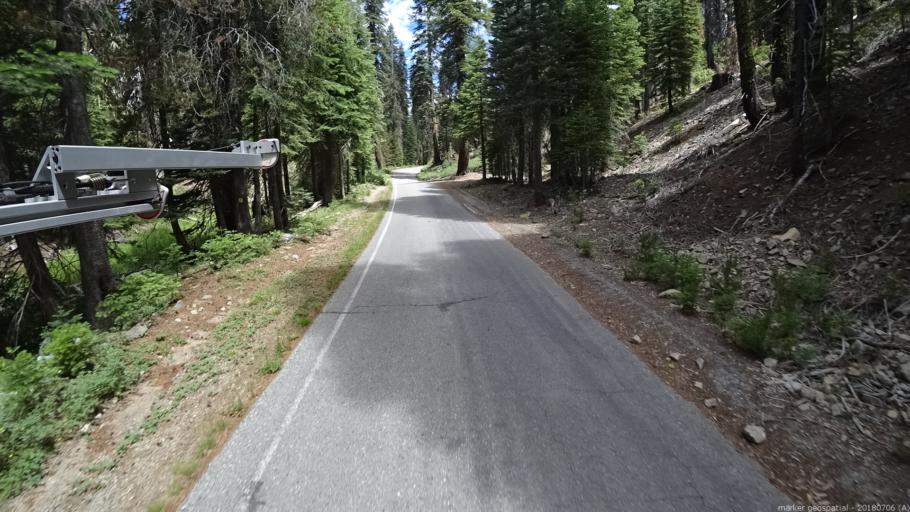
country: US
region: California
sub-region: Madera County
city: Oakhurst
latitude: 37.4294
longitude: -119.4311
